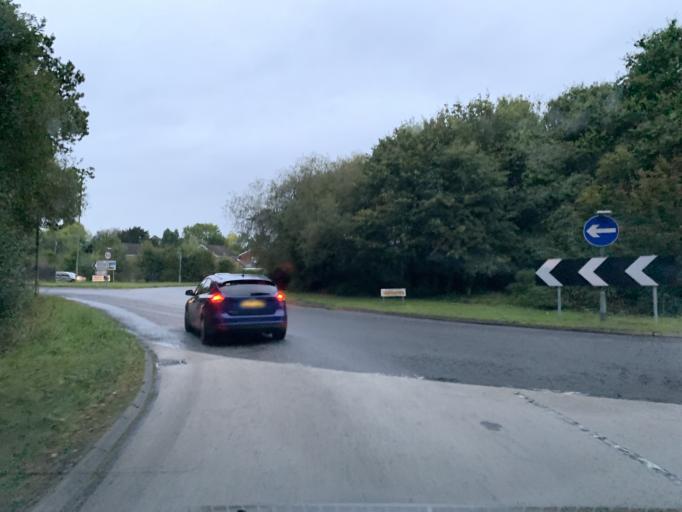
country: GB
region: England
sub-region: Hampshire
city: Cadnam
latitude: 50.9202
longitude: -1.5819
